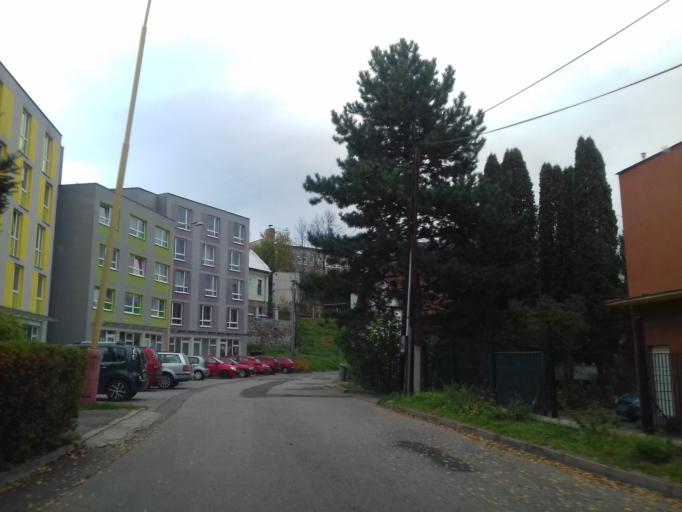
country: SK
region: Zilinsky
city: Ruzomberok
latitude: 49.0795
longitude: 19.3024
